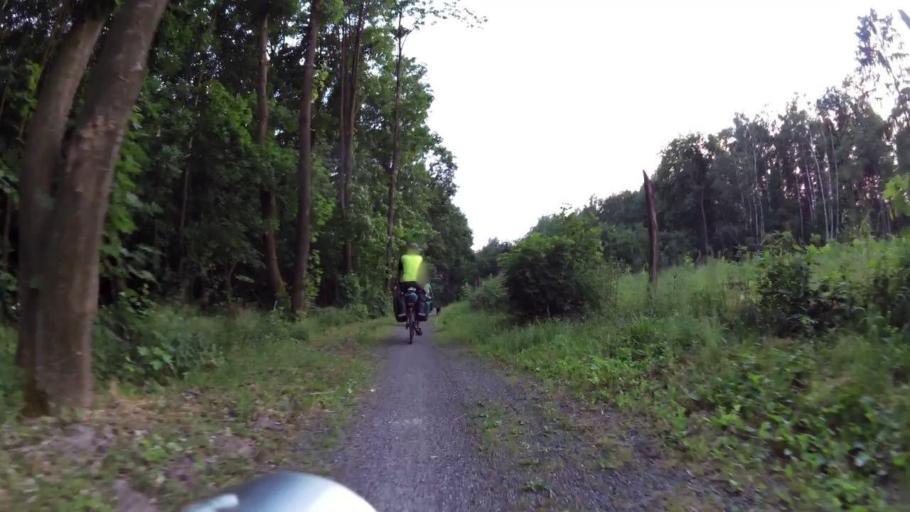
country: PL
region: Kujawsko-Pomorskie
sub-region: Powiat bydgoski
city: Dabrowa Chelminska
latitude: 53.1692
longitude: 18.2608
